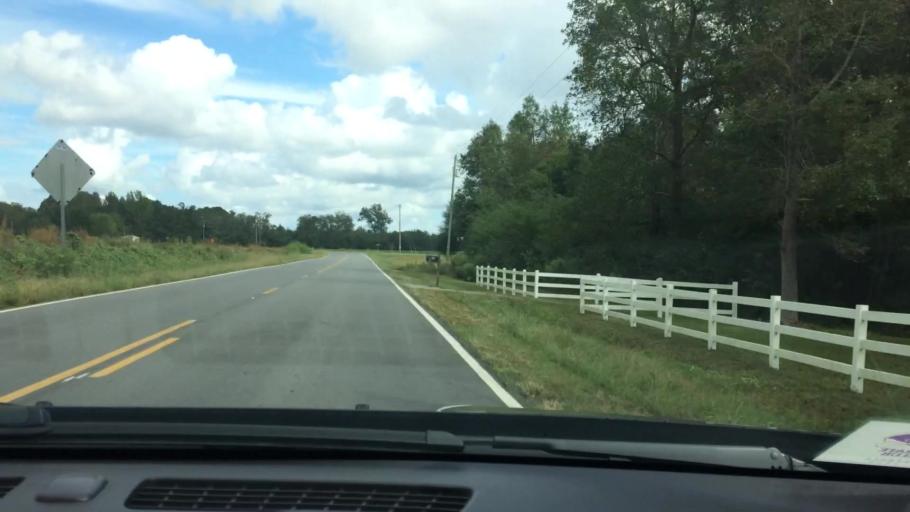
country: US
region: North Carolina
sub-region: Pitt County
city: Ayden
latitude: 35.4574
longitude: -77.4722
